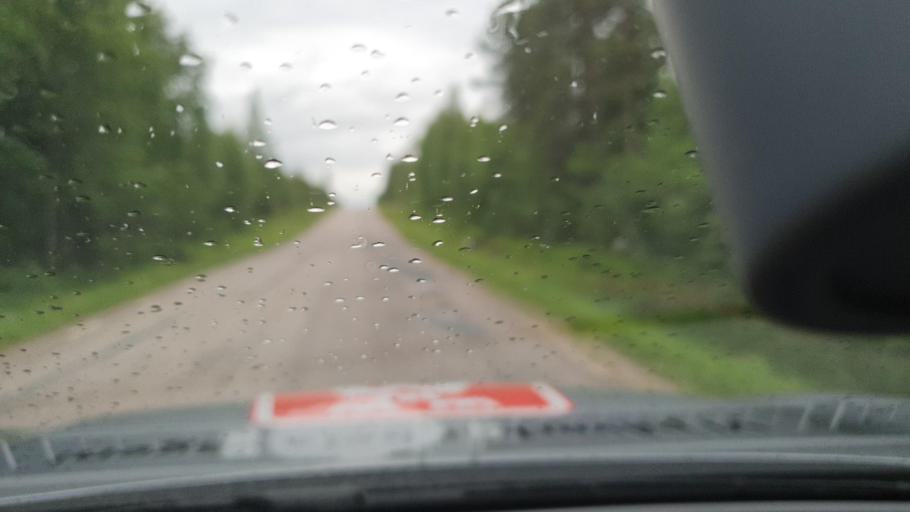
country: SE
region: Norrbotten
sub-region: Overkalix Kommun
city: OEverkalix
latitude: 66.3730
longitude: 22.7986
